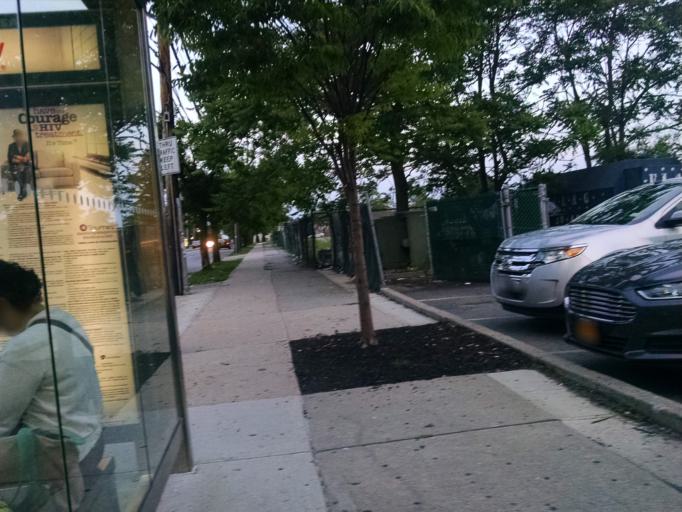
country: US
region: New York
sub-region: Richmond County
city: Staten Island
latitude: 40.5696
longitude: -74.1084
